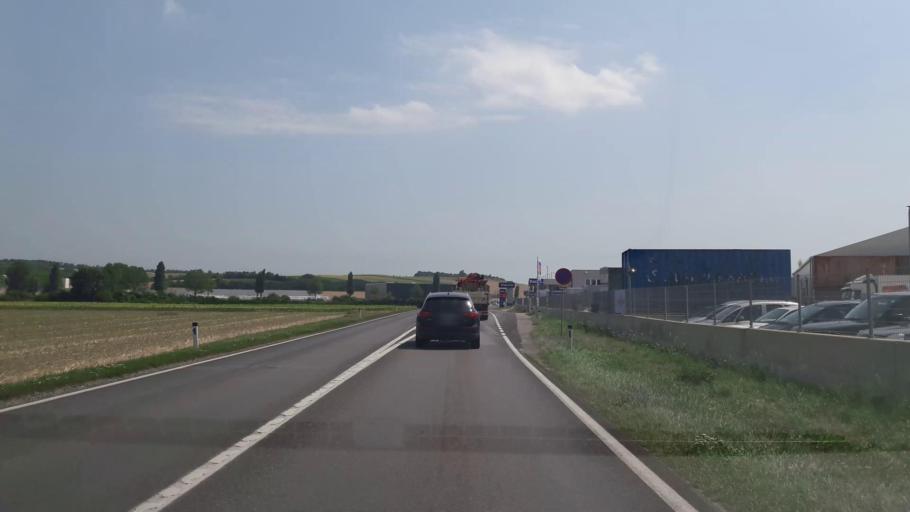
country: AT
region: Lower Austria
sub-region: Politischer Bezirk Bruck an der Leitha
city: Enzersdorf an der Fischa
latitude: 48.0671
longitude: 16.6023
